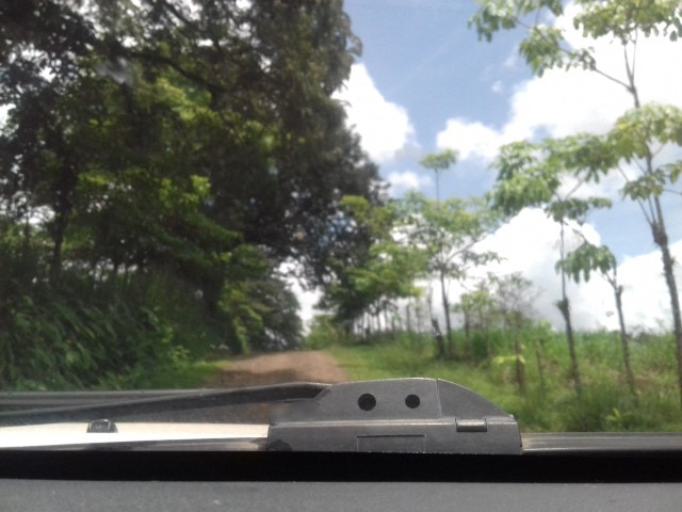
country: NI
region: Matagalpa
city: Rio Blanco
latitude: 12.9934
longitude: -85.3840
